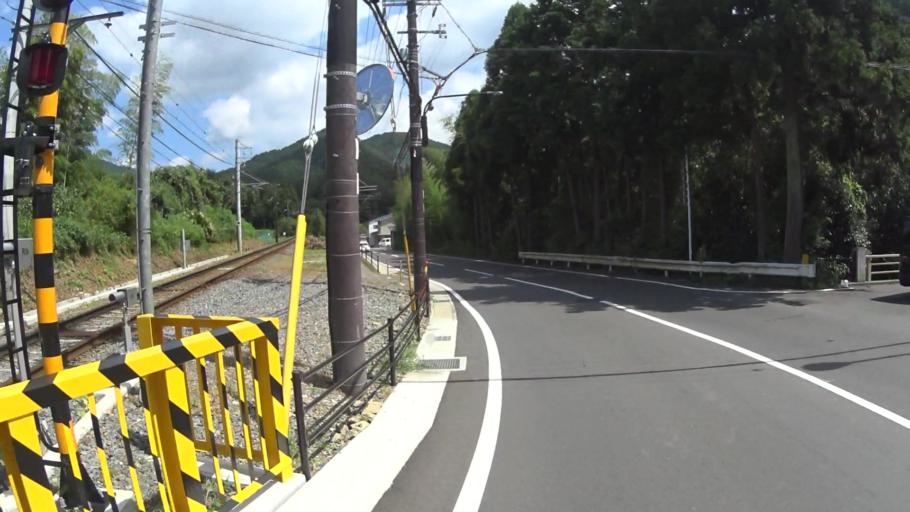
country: JP
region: Kyoto
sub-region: Kyoto-shi
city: Kamigyo-ku
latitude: 35.0908
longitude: 135.7653
